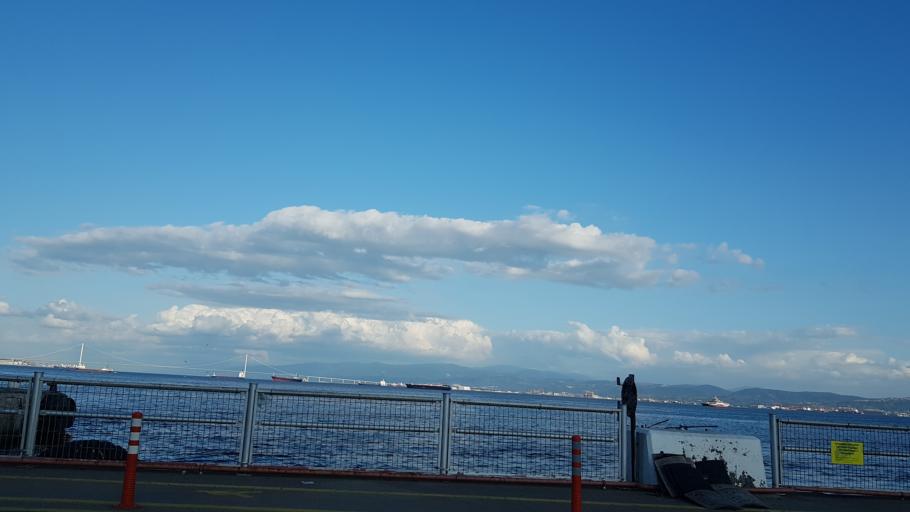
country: TR
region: Kocaeli
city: Darica
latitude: 40.7658
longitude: 29.4224
